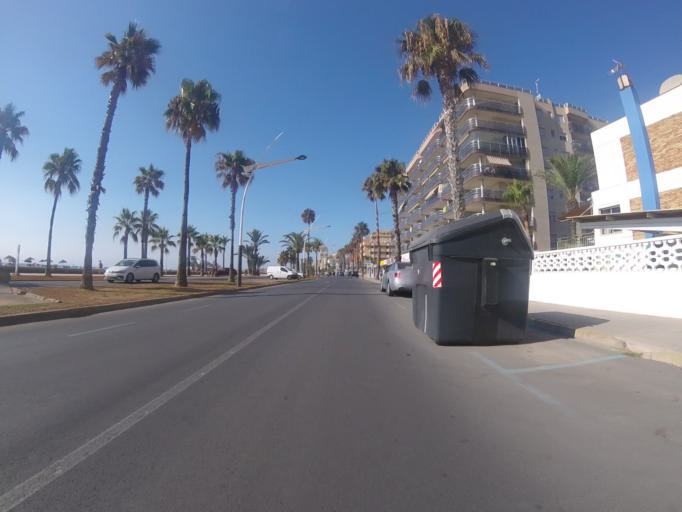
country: ES
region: Valencia
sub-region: Provincia de Castello
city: Peniscola
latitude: 40.3717
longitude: 0.4050
